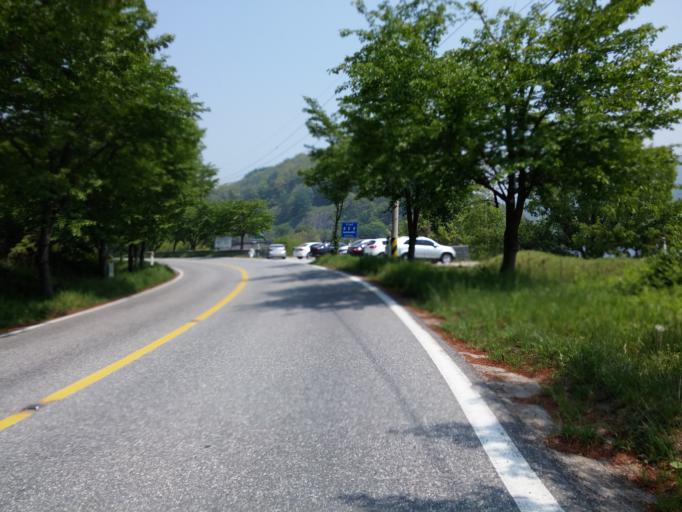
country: KR
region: Chungcheongbuk-do
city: Okcheon
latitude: 36.4398
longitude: 127.5725
